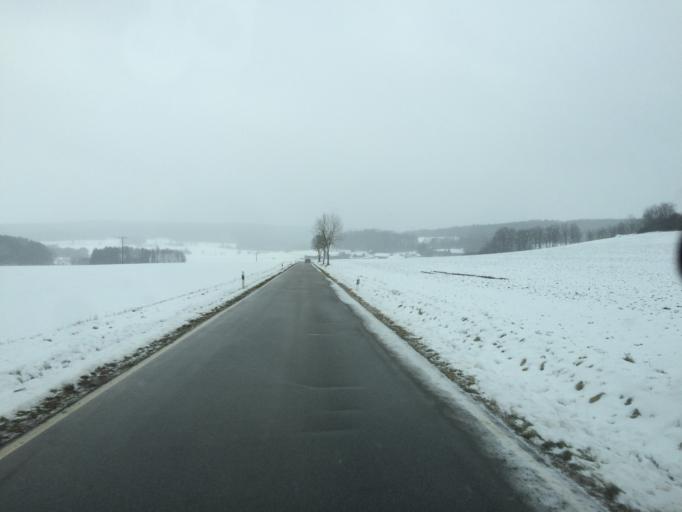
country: DE
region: Bavaria
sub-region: Upper Palatinate
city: Breitenbrunn
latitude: 49.3608
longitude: 12.0166
